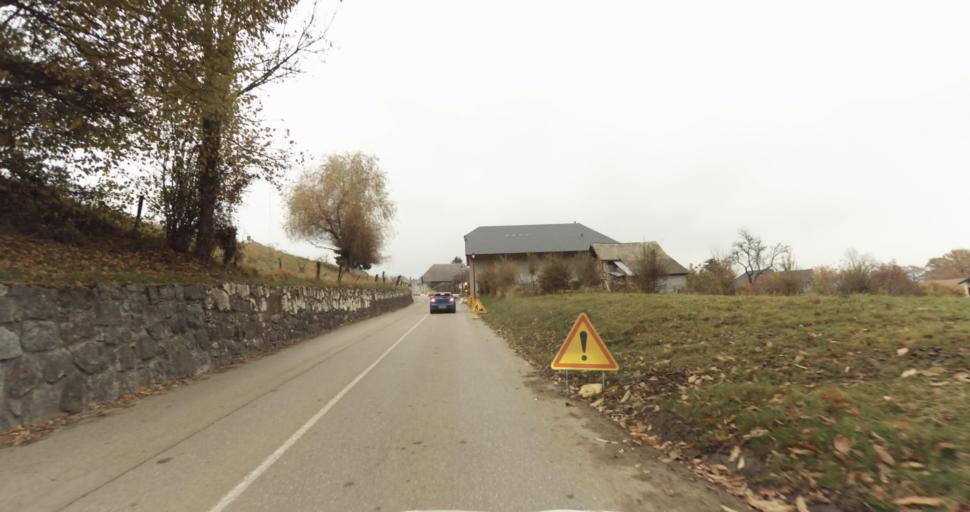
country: FR
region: Rhone-Alpes
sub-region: Departement de la Haute-Savoie
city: Alby-sur-Cheran
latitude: 45.7937
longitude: 6.0114
